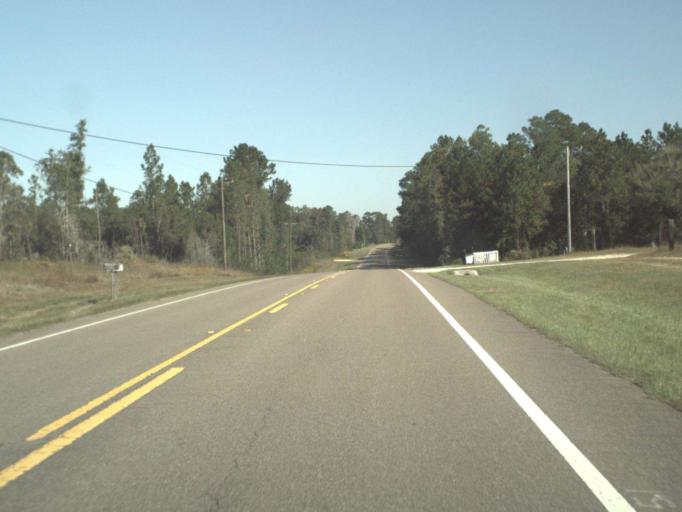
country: US
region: Florida
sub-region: Walton County
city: Freeport
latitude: 30.5300
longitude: -85.9233
